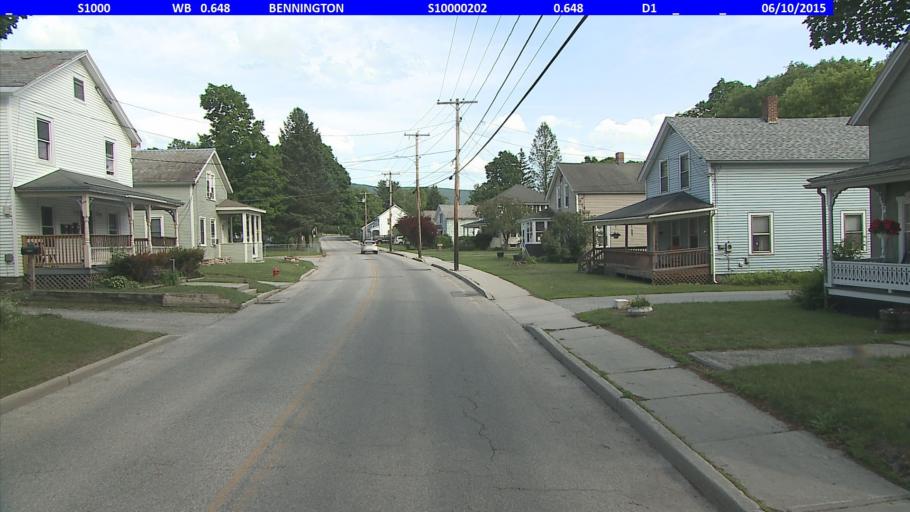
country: US
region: Vermont
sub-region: Bennington County
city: Bennington
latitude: 42.8762
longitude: -73.1838
